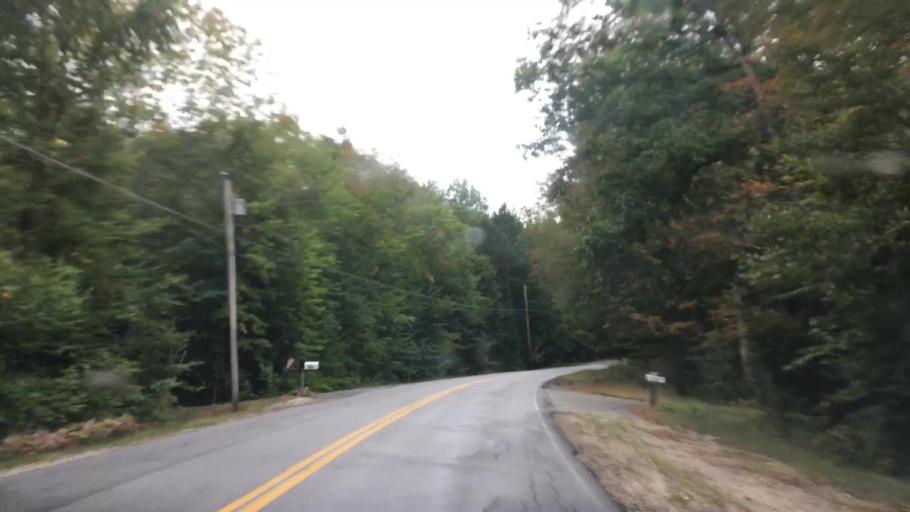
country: US
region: Maine
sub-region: Cumberland County
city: Raymond
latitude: 43.9346
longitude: -70.4199
